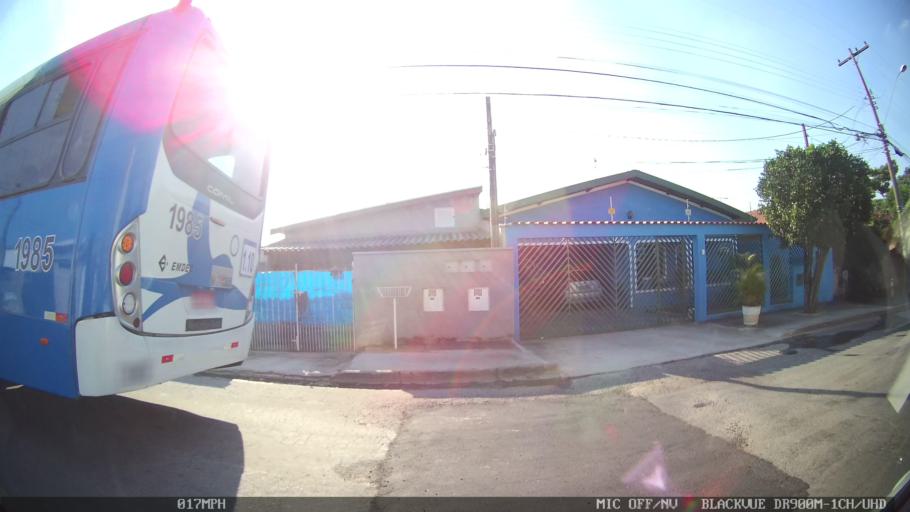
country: BR
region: Sao Paulo
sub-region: Campinas
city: Campinas
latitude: -22.9847
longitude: -47.1496
